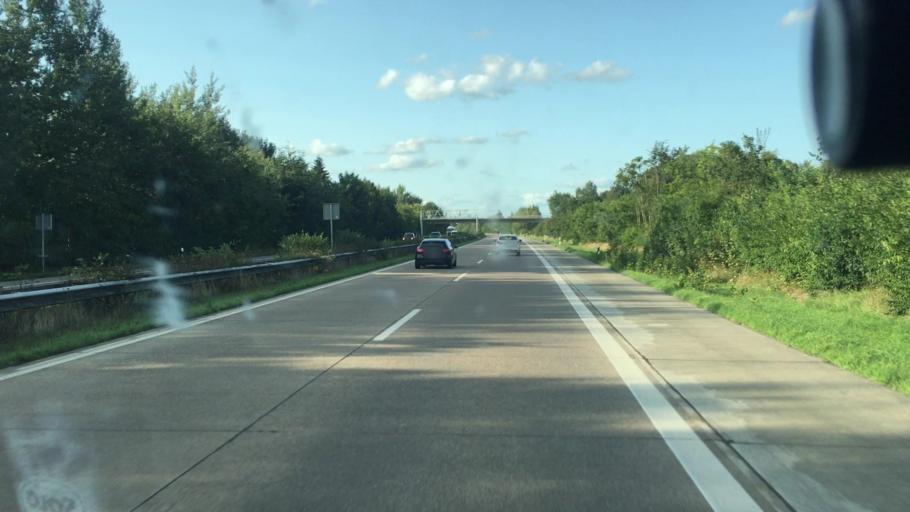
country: DE
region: Lower Saxony
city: Wiefelstede
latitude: 53.3024
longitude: 8.1457
